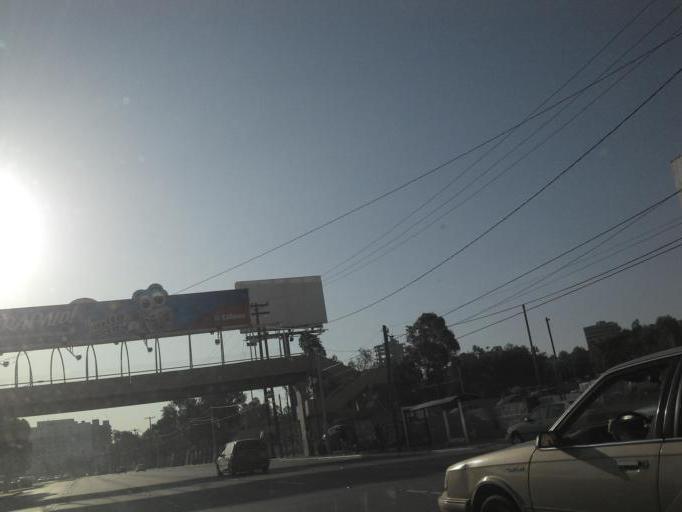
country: MX
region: Baja California
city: Tijuana
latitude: 32.5125
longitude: -117.0038
